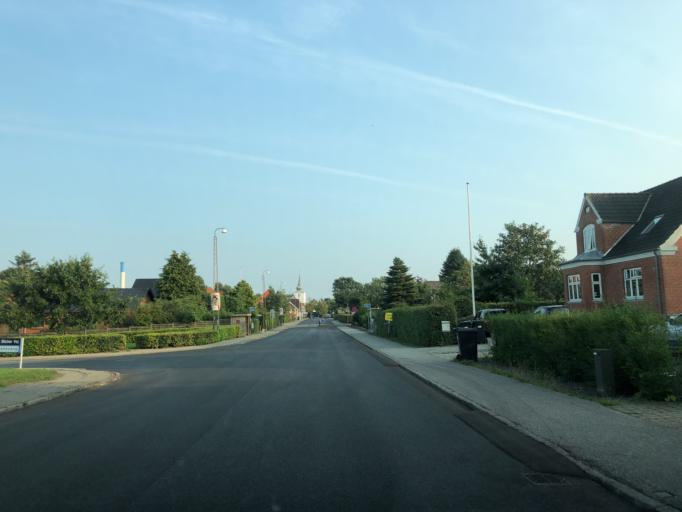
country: DK
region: South Denmark
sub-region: Vejle Kommune
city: Jelling
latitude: 55.7050
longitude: 9.3780
